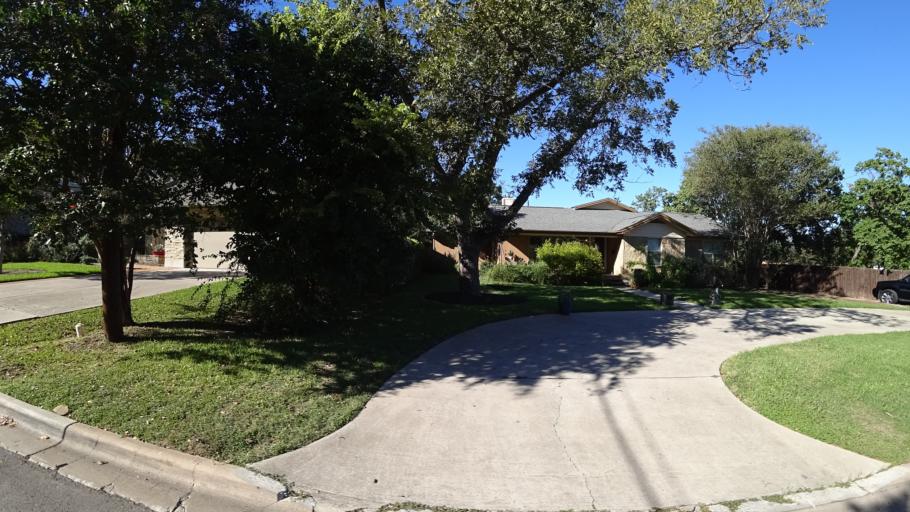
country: US
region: Texas
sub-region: Travis County
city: West Lake Hills
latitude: 30.3293
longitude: -97.7607
